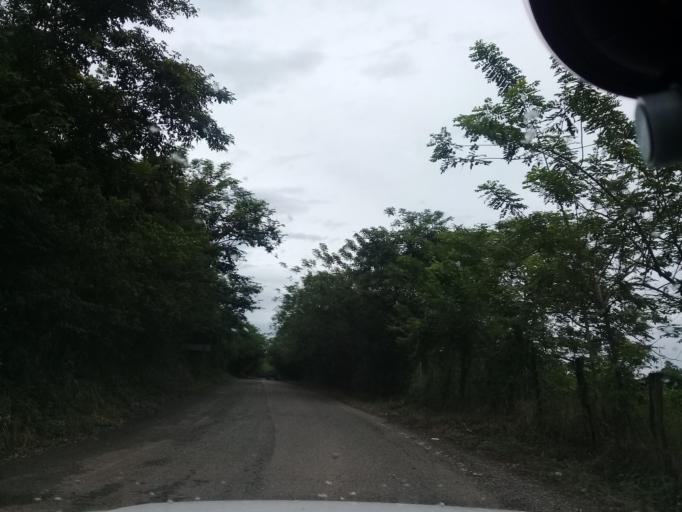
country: MX
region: Veracruz
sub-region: Chalma
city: San Pedro Coyutla
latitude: 21.2090
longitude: -98.3857
